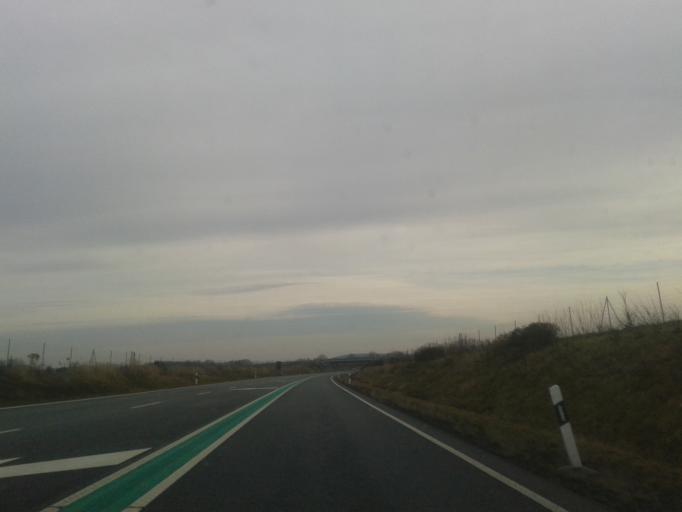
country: DE
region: Saxony
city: Eibau
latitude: 50.9958
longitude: 14.7003
